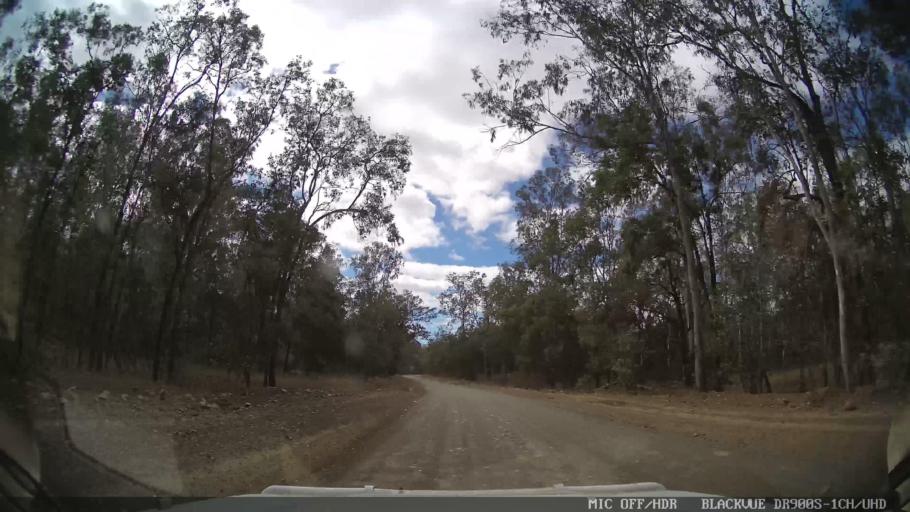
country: AU
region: Queensland
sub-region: Gladstone
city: Toolooa
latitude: -24.5497
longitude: 151.3422
